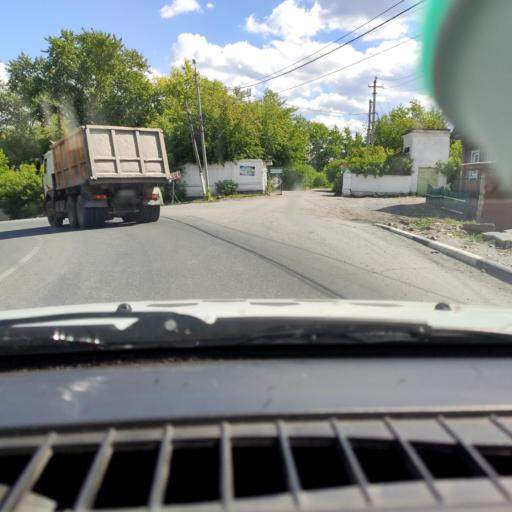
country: RU
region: Chelyabinsk
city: Satka
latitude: 55.0343
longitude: 59.0228
